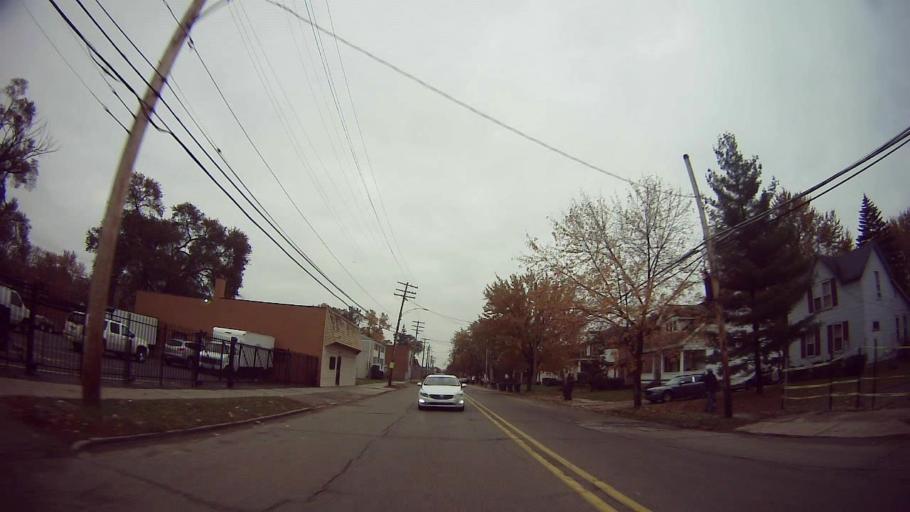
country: US
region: Michigan
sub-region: Wayne County
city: Redford
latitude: 42.4211
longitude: -83.2580
